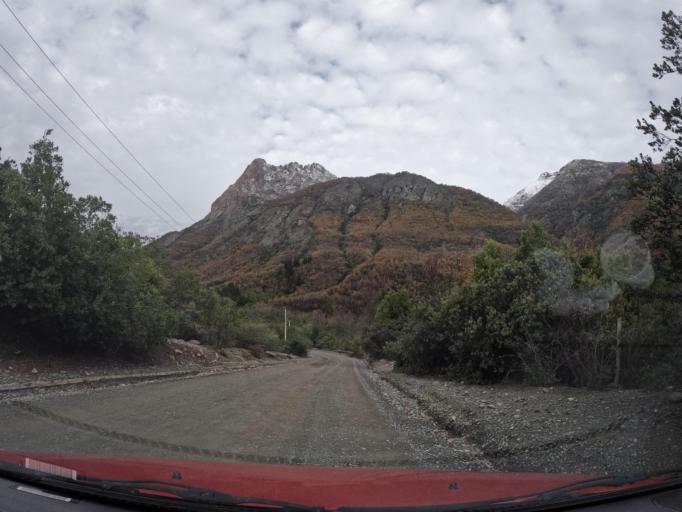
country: CL
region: Maule
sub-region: Provincia de Linares
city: Colbun
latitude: -35.8559
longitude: -71.2042
